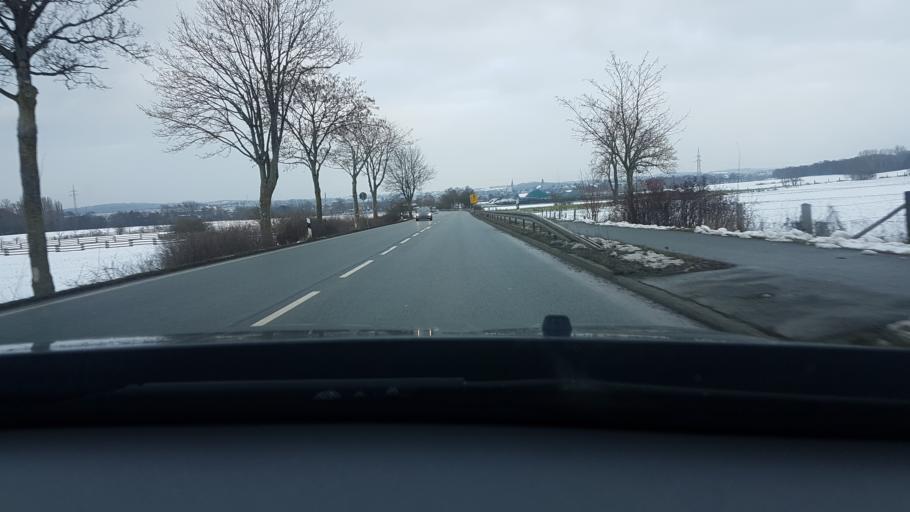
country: DE
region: Hesse
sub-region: Regierungsbezirk Kassel
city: Korbach
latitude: 51.2879
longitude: 8.8325
